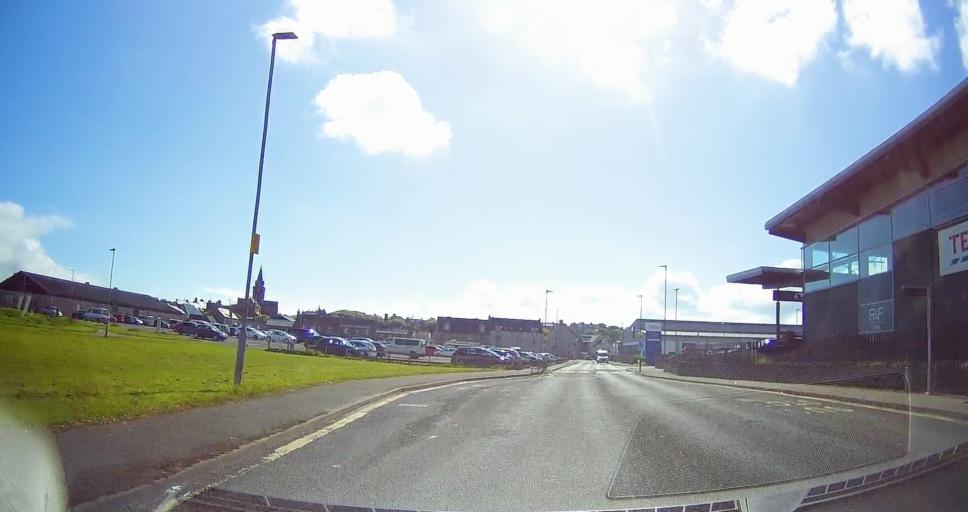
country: GB
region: Scotland
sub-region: Orkney Islands
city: Orkney
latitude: 58.9812
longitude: -2.9676
